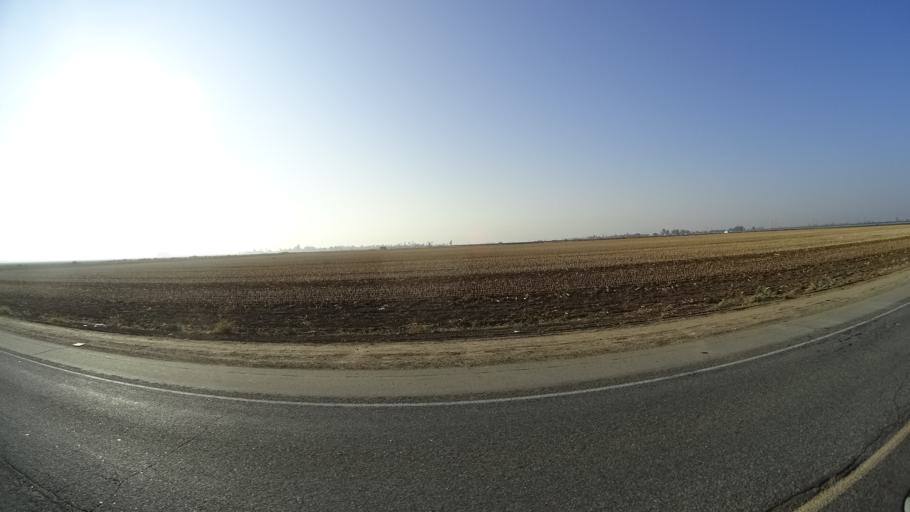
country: US
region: California
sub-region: Kern County
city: Greenfield
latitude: 35.2669
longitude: -118.9692
